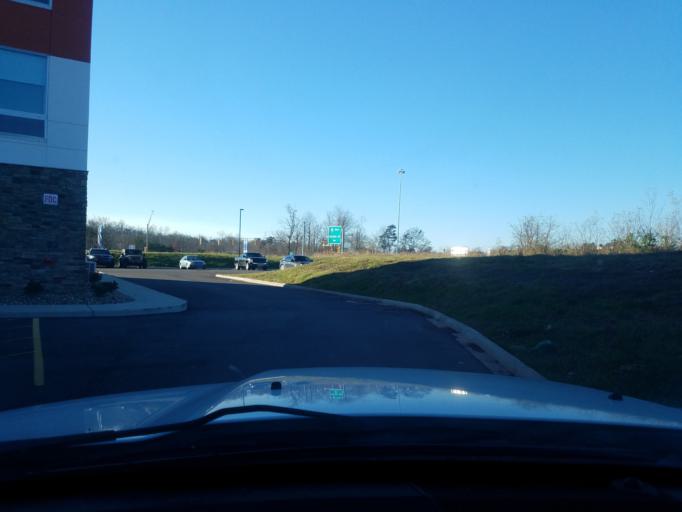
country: US
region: West Virginia
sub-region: Wood County
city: Boaz
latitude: 39.3148
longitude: -81.4763
